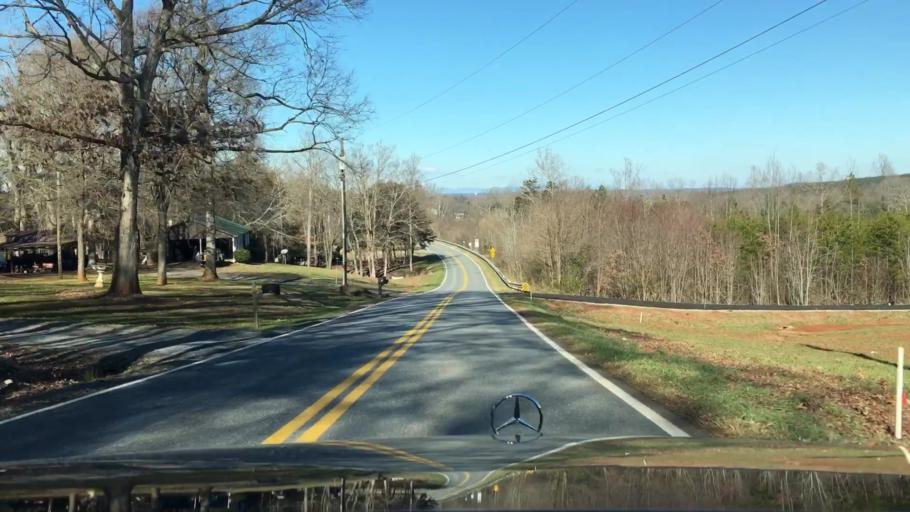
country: US
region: Virginia
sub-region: Campbell County
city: Altavista
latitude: 37.1550
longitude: -79.2977
